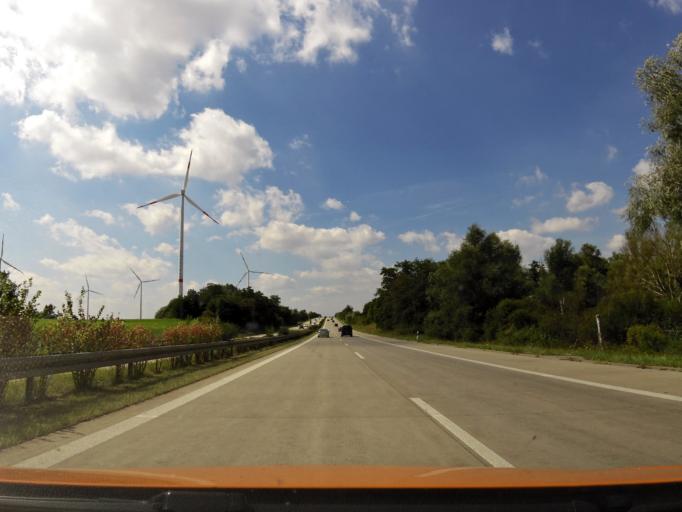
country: PL
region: West Pomeranian Voivodeship
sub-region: Powiat policki
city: Kolbaskowo
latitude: 53.3316
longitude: 14.3796
